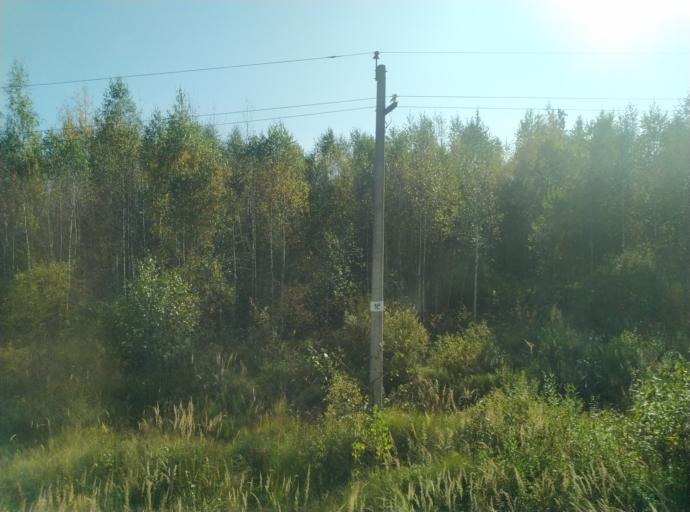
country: RU
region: Moskovskaya
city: Novo-Nikol'skoye
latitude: 56.5429
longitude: 37.5493
